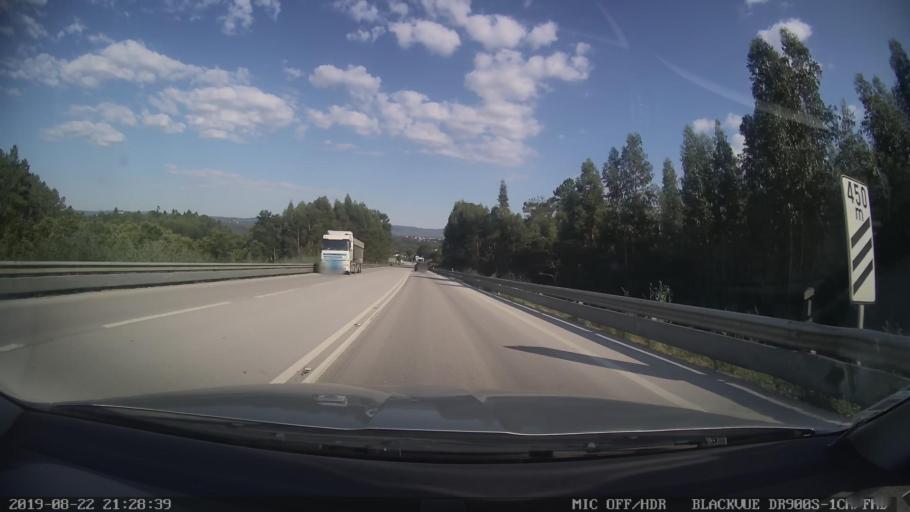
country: PT
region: Leiria
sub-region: Pedrogao Grande
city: Pedrogao Grande
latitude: 39.8953
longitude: -8.1229
